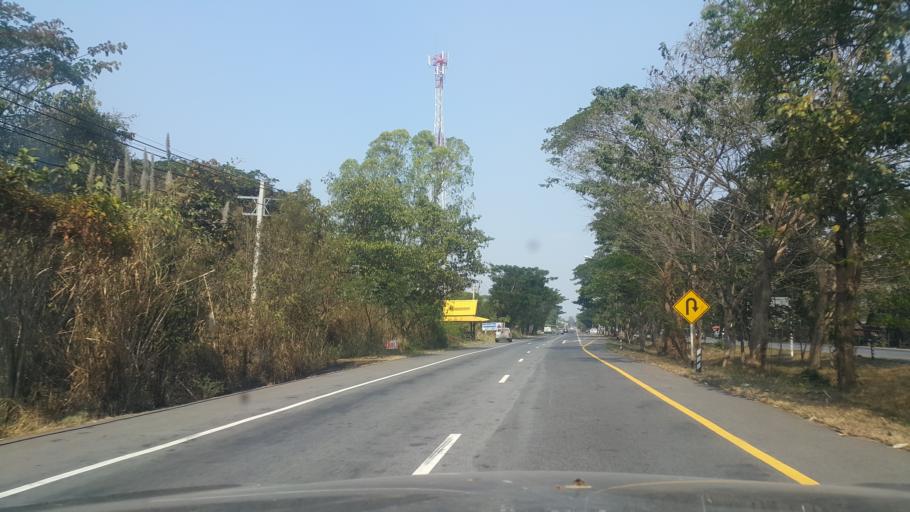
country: TH
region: Nakhon Ratchasima
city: Wang Nam Khiao
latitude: 14.5100
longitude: 101.9549
